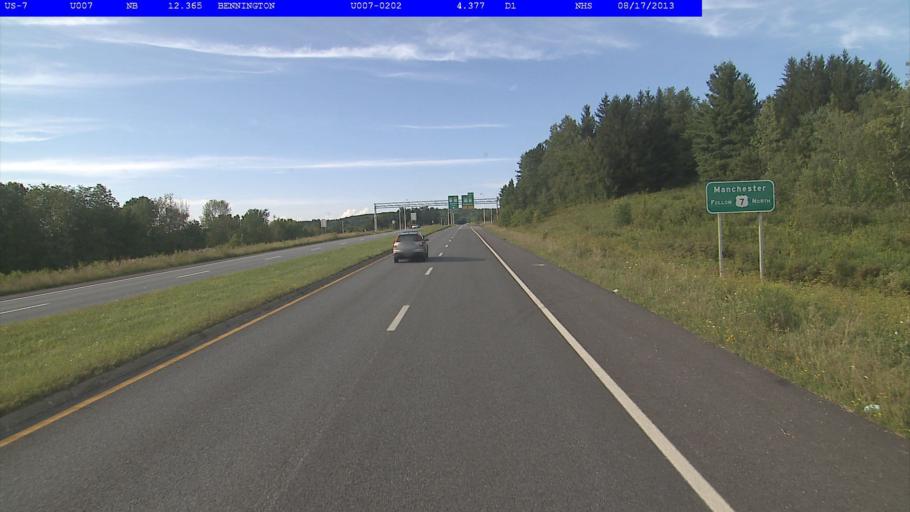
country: US
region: Vermont
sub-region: Bennington County
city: Bennington
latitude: 42.8975
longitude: -73.1997
